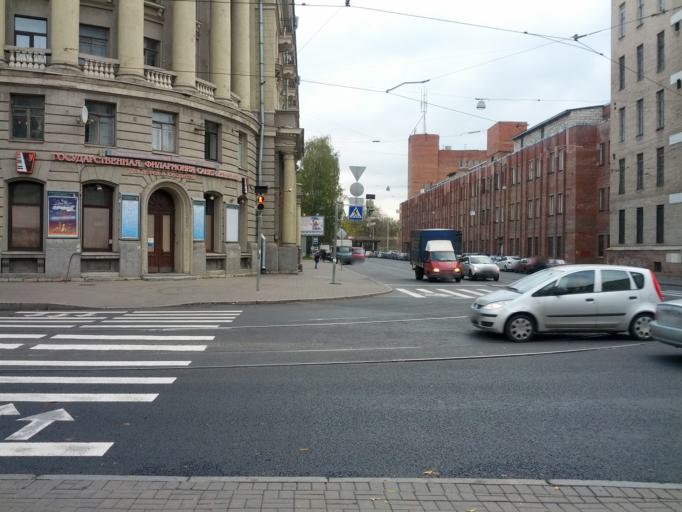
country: RU
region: Leningrad
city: Sampsonievskiy
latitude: 59.9884
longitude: 30.3334
